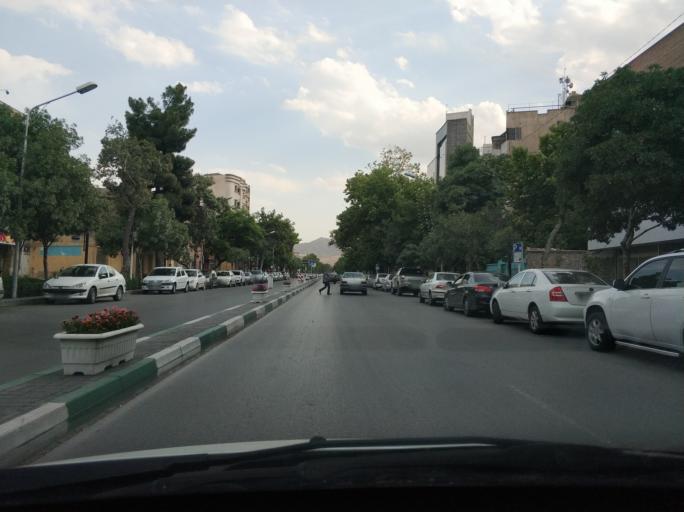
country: IR
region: Razavi Khorasan
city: Mashhad
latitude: 36.2831
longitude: 59.5970
